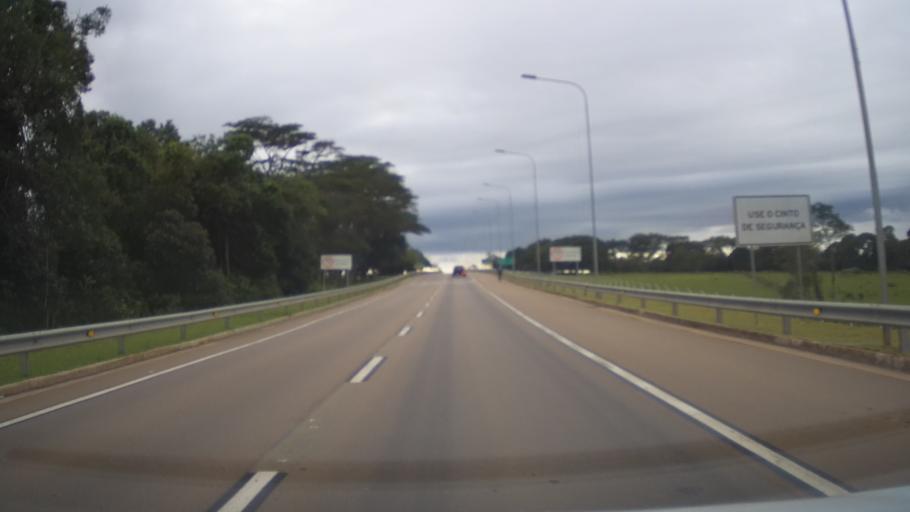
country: BR
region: Sao Paulo
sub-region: Indaiatuba
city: Indaiatuba
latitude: -23.0187
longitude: -47.1353
